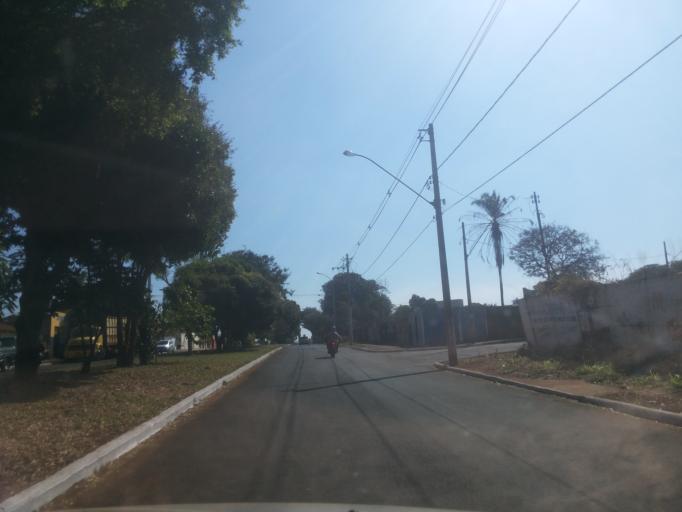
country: BR
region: Minas Gerais
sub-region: Ituiutaba
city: Ituiutaba
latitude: -18.9696
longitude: -49.4516
